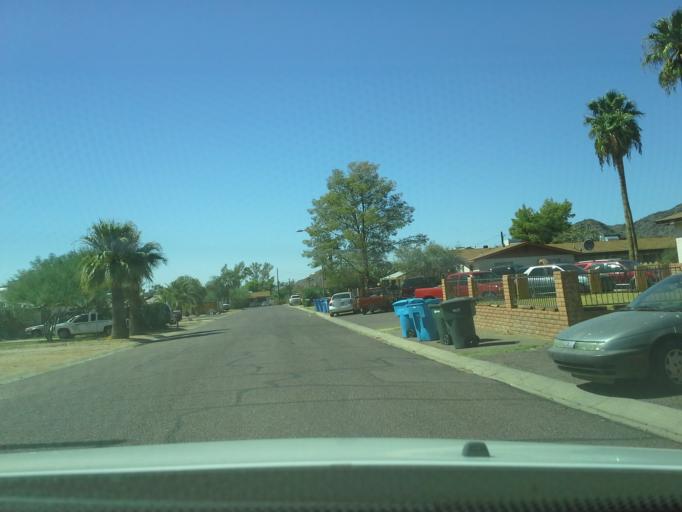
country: US
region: Arizona
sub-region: Maricopa County
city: Paradise Valley
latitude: 33.5727
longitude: -112.0528
